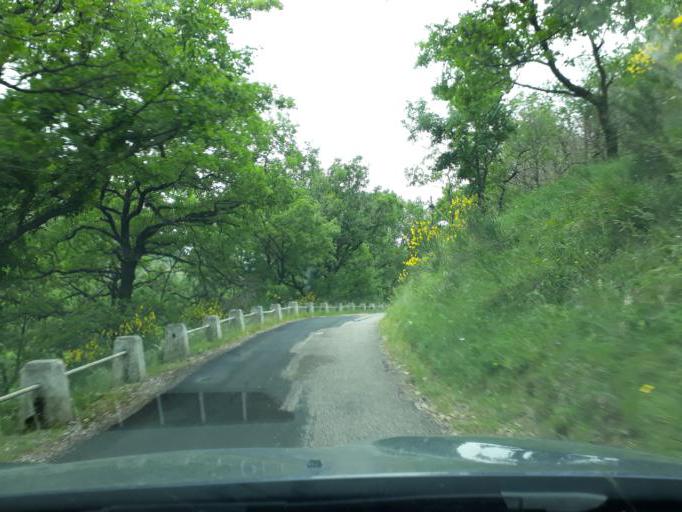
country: FR
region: Languedoc-Roussillon
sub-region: Departement de l'Herault
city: Lodeve
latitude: 43.7904
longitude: 3.2790
